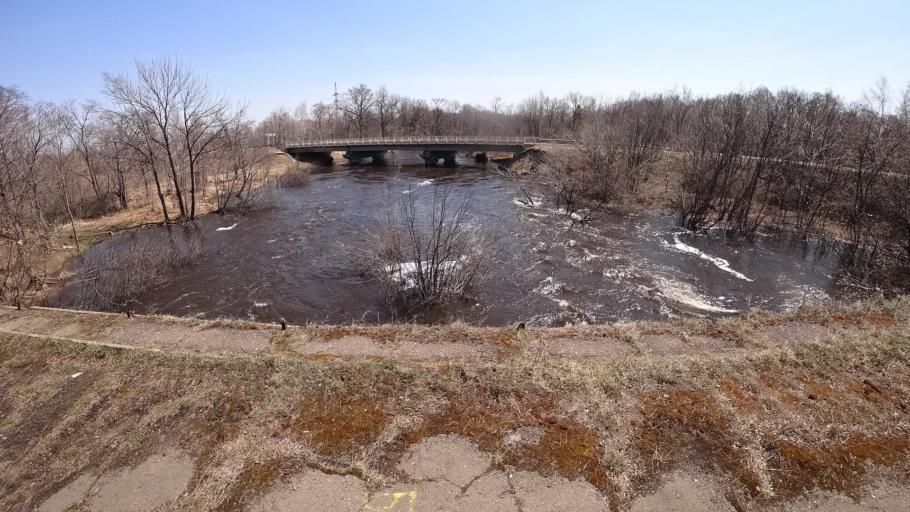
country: RU
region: Khabarovsk Krai
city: Khurba
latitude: 50.4002
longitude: 136.8648
